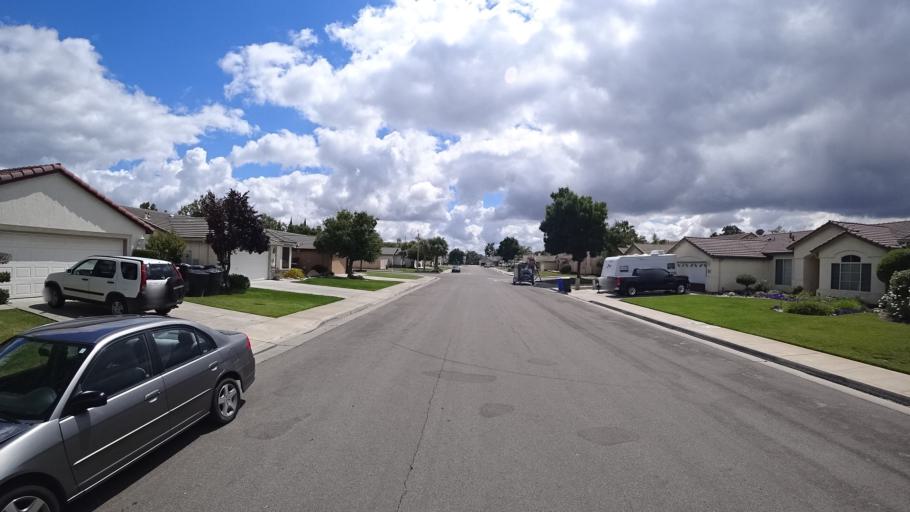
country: US
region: California
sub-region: Kings County
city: Lucerne
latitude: 36.3578
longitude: -119.6578
